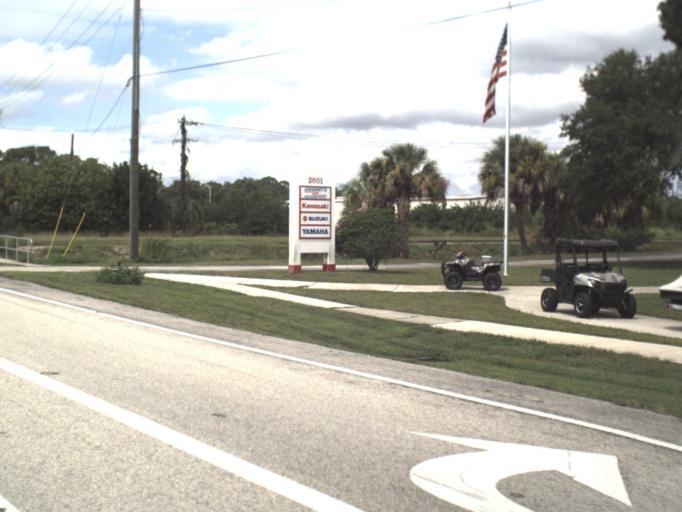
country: US
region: Florida
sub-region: Sarasota County
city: North Sarasota
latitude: 27.3888
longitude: -82.5298
